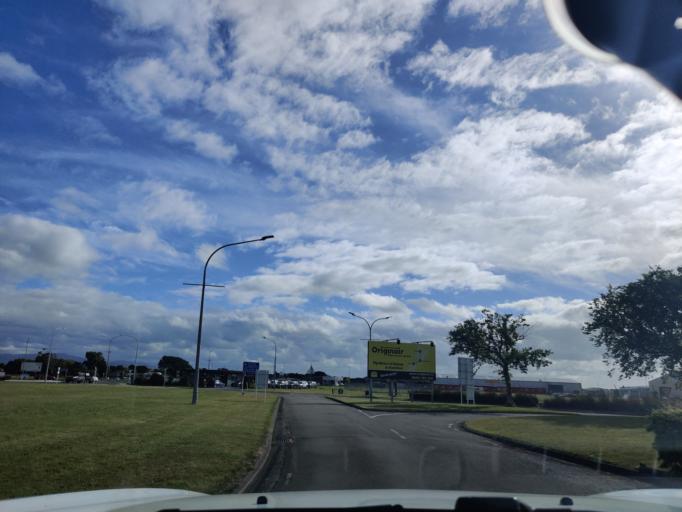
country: NZ
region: Manawatu-Wanganui
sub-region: Palmerston North City
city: Palmerston North
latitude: -40.3248
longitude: 175.6213
